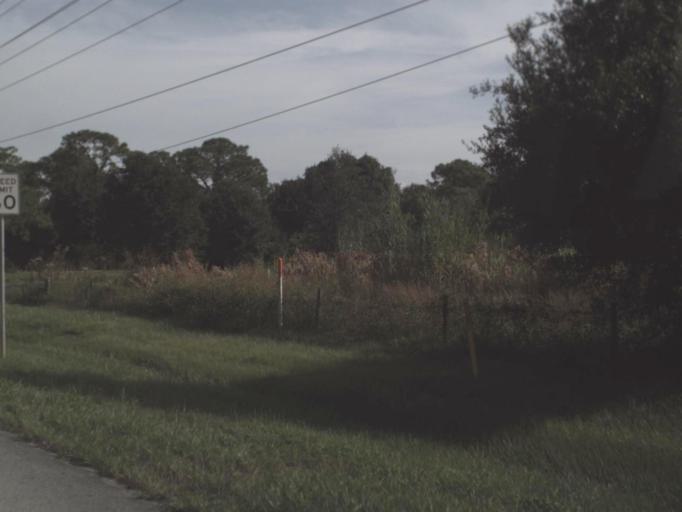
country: US
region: Florida
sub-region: Lee County
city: Fort Myers Shores
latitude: 26.7275
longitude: -81.7610
